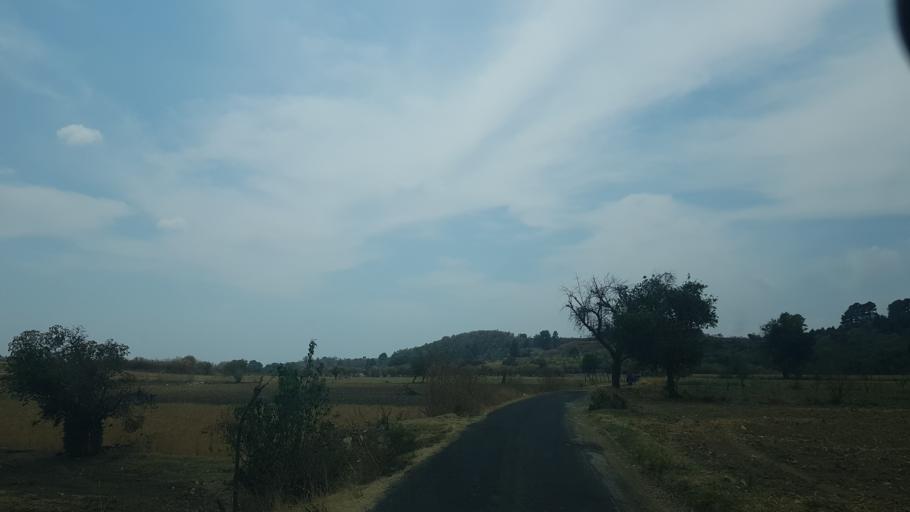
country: MX
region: Puebla
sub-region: Atzitzihuacan
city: Santiago Atzitzihuacan
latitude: 18.8552
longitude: -98.6116
